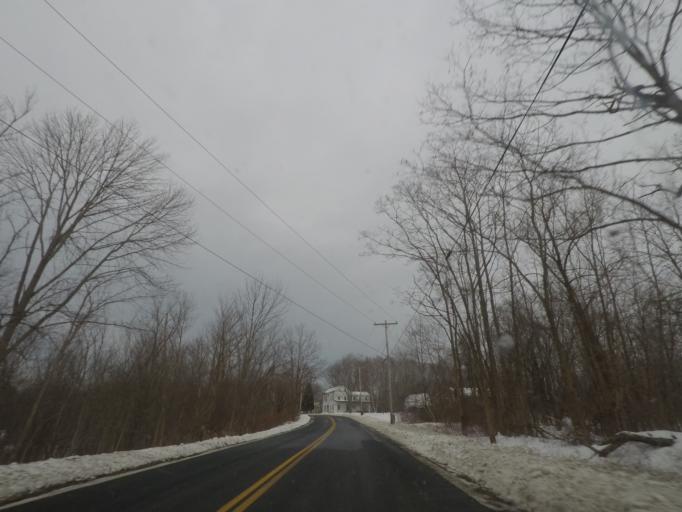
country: US
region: New York
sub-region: Rensselaer County
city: Castleton-on-Hudson
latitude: 42.5138
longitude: -73.7248
